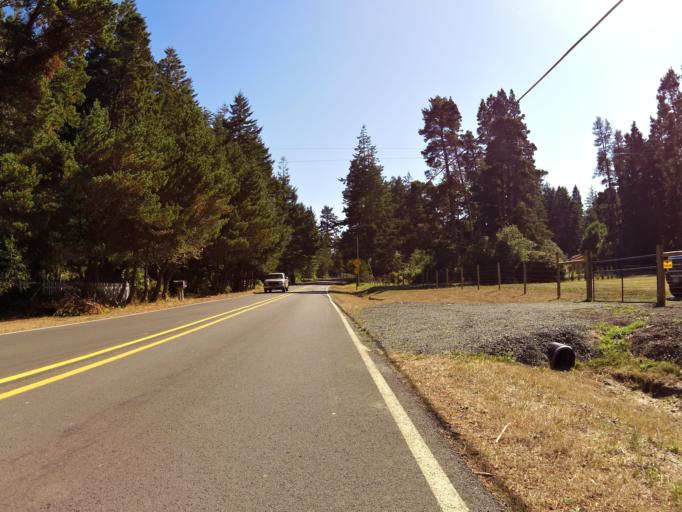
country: US
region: Oregon
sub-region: Coos County
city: Bandon
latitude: 43.2128
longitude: -124.3698
